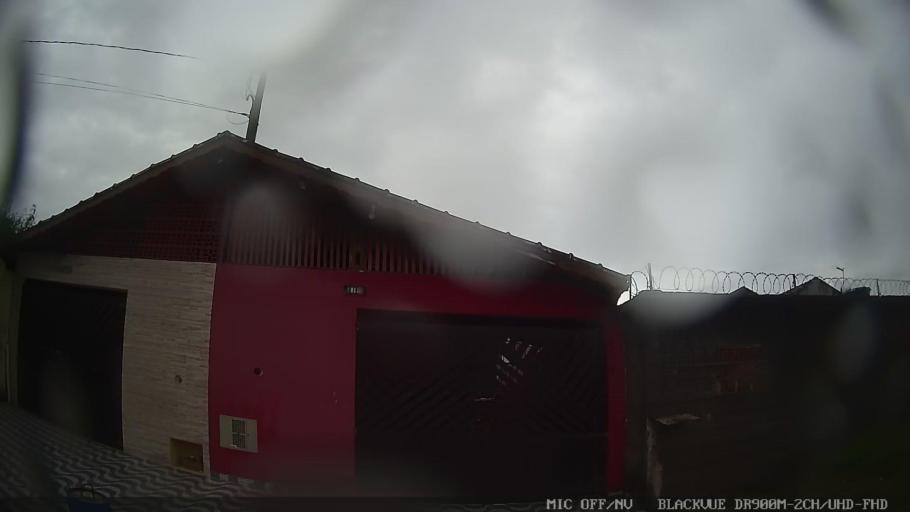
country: BR
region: Sao Paulo
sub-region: Mongagua
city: Mongagua
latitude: -24.1317
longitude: -46.6936
